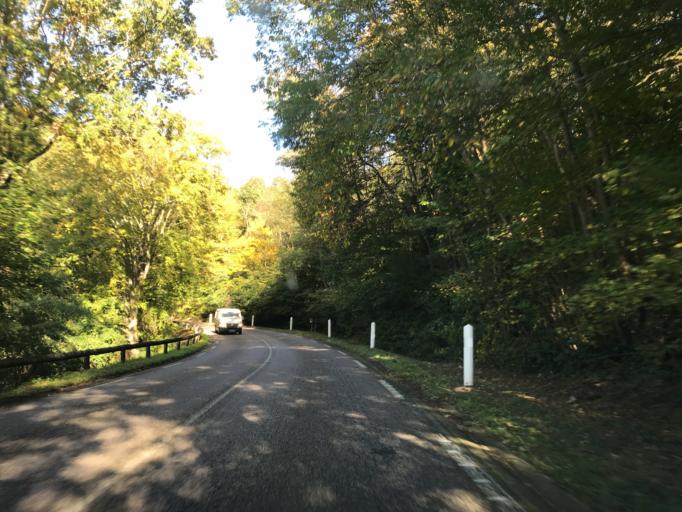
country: FR
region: Haute-Normandie
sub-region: Departement de l'Eure
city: Saint-Aubin-sur-Gaillon
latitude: 49.1054
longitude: 1.2924
